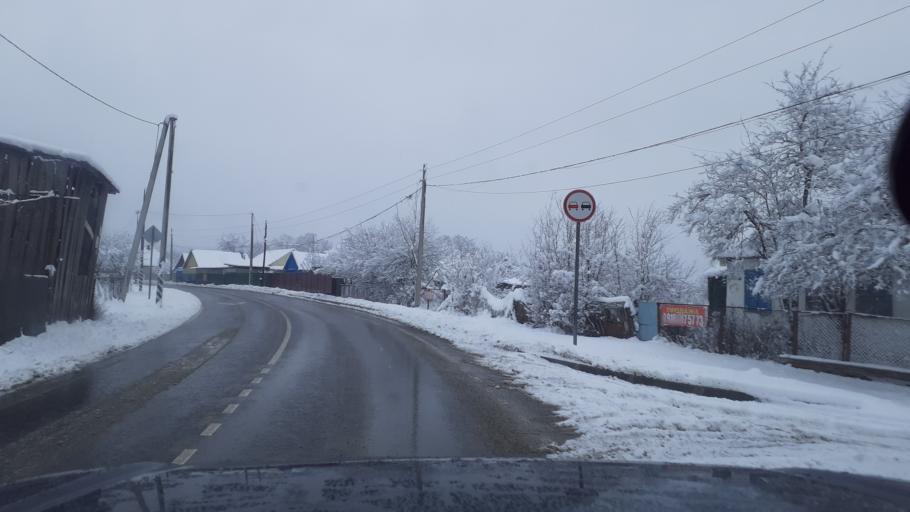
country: RU
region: Adygeya
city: Kamennomostskiy
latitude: 44.2278
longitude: 40.2025
